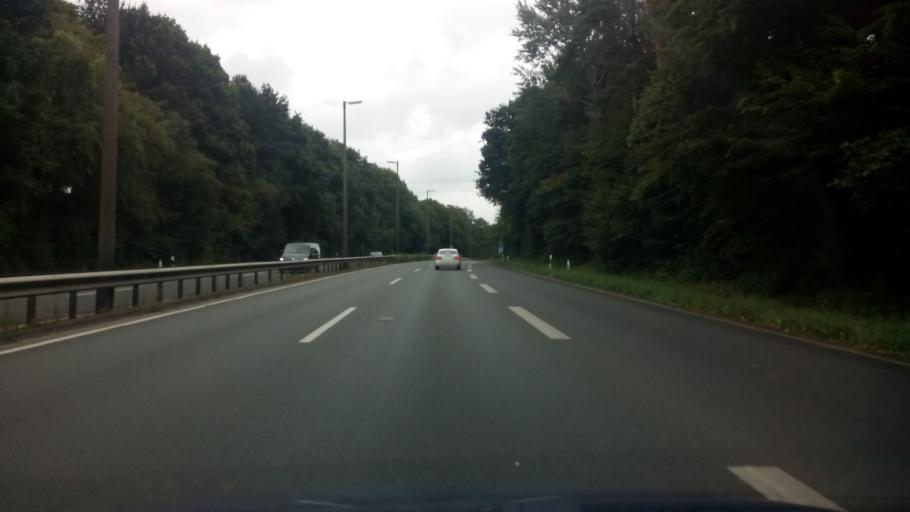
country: DE
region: Lower Saxony
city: Lemwerder
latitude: 53.1747
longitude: 8.6431
